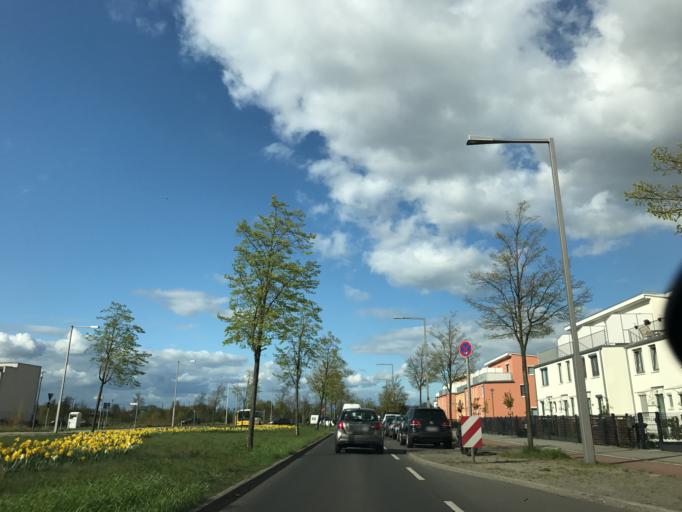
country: DE
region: Berlin
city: Haselhorst
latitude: 52.5558
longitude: 13.2262
